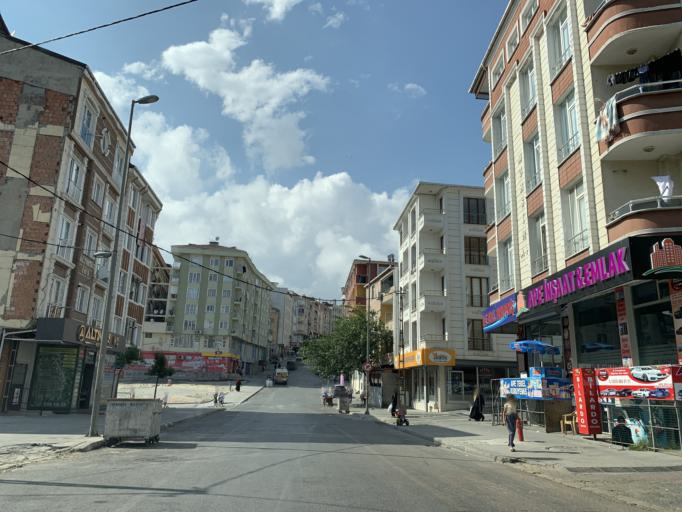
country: TR
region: Istanbul
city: Esenyurt
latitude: 41.0337
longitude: 28.6694
